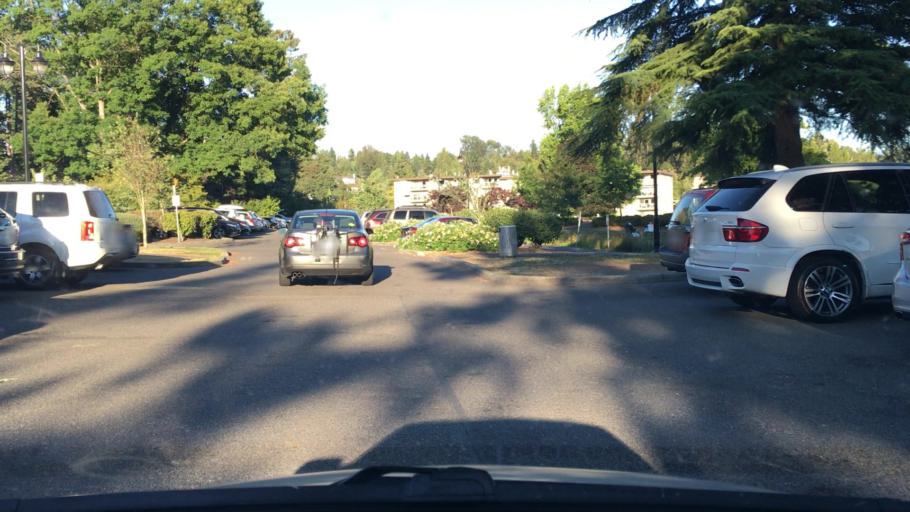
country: US
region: Washington
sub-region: King County
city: Inglewood-Finn Hill
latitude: 47.7049
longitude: -122.2159
